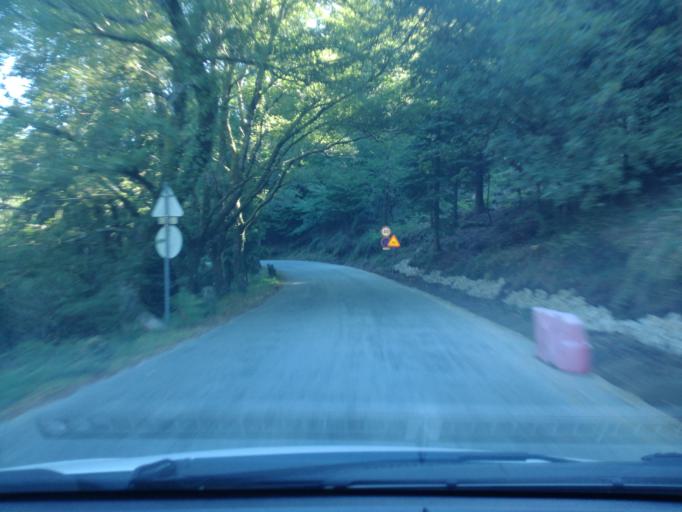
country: ES
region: Galicia
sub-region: Provincia de Ourense
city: Lobios
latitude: 41.7676
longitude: -8.1466
